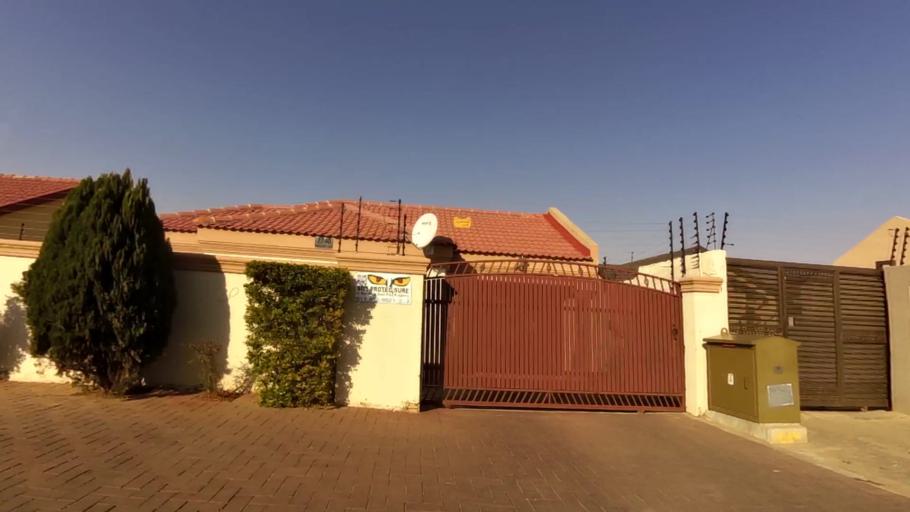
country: ZA
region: Gauteng
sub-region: City of Johannesburg Metropolitan Municipality
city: Soweto
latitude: -26.2939
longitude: 27.9479
